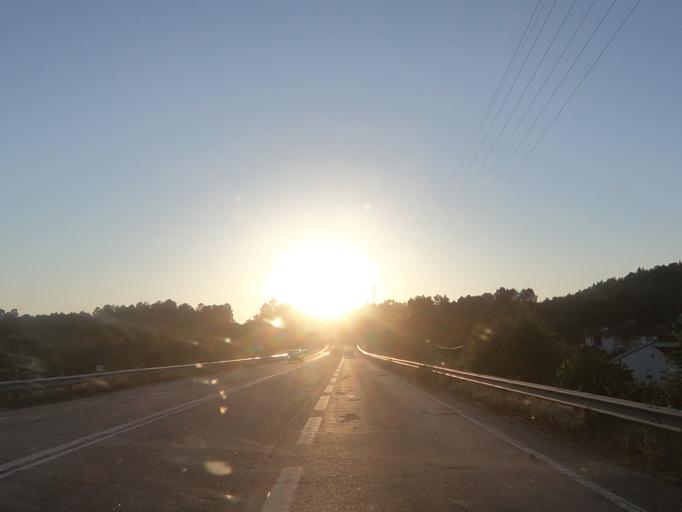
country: PT
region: Viseu
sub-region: Viseu
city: Rio de Loba
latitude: 40.6815
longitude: -7.8841
